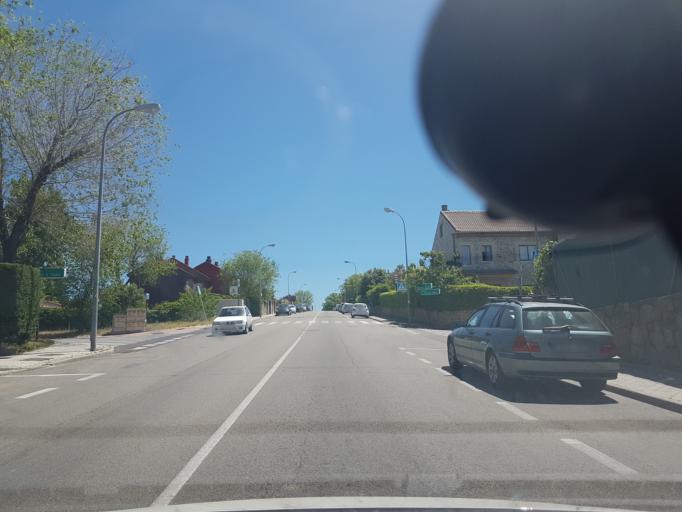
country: ES
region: Madrid
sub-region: Provincia de Madrid
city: Pozuelo de Alarcon
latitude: 40.4403
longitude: -3.8050
